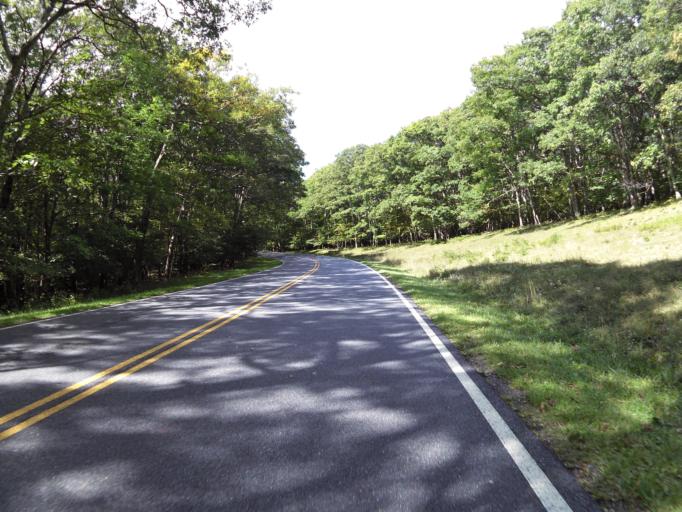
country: US
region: Virginia
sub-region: Page County
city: Luray
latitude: 38.5917
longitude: -78.3724
